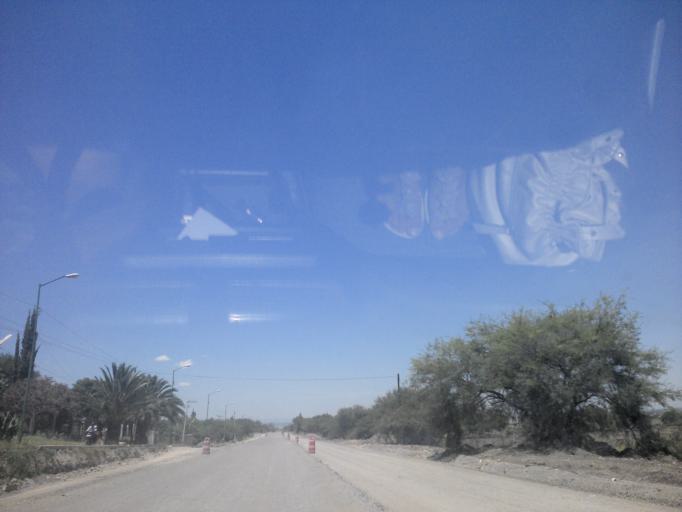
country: MX
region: Guanajuato
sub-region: San Francisco del Rincon
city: San Ignacio de Hidalgo
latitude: 20.9417
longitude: -101.9094
